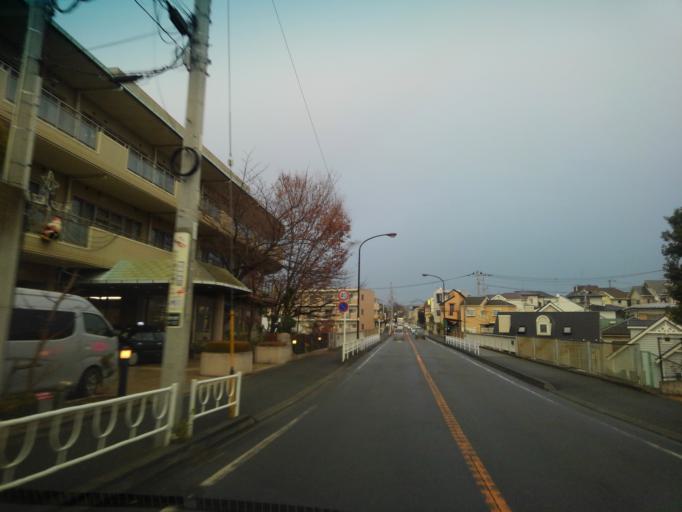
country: JP
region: Tokyo
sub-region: Machida-shi
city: Machida
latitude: 35.5262
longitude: 139.4401
